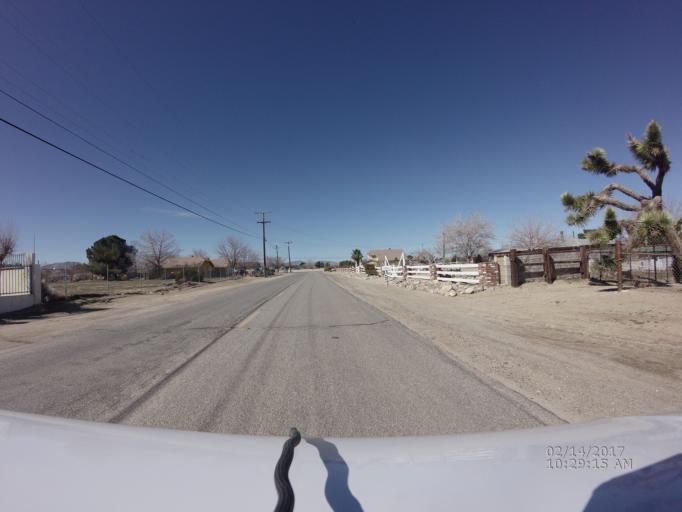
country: US
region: California
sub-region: Los Angeles County
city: Littlerock
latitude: 34.5598
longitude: -117.9506
